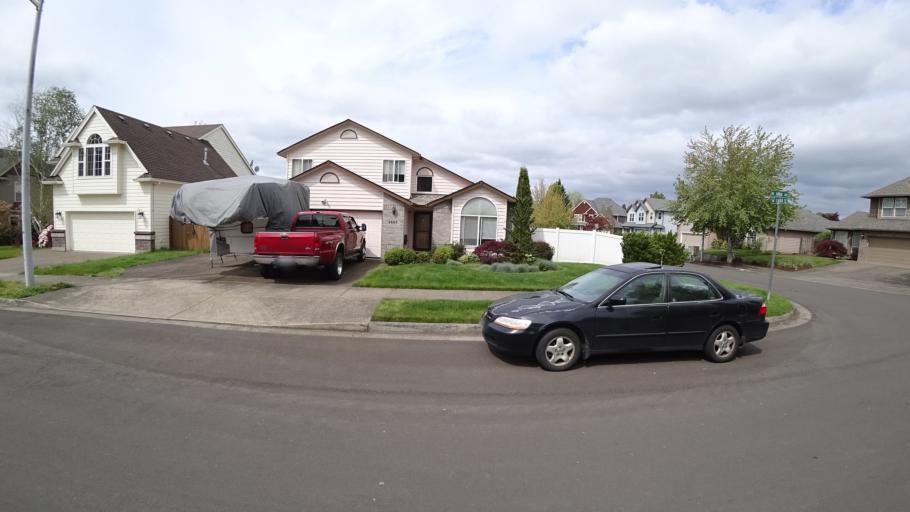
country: US
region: Oregon
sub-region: Washington County
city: Hillsboro
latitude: 45.5449
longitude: -122.9900
